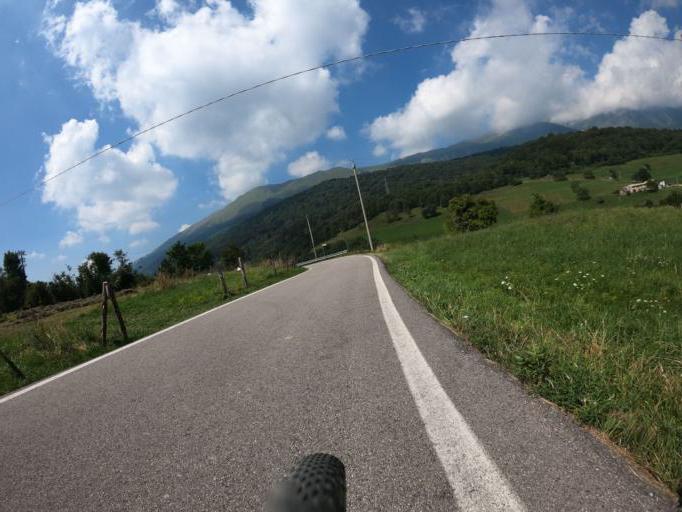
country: IT
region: Veneto
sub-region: Provincia di Verona
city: Ferrara di Monte Baldo
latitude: 45.6597
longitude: 10.8488
